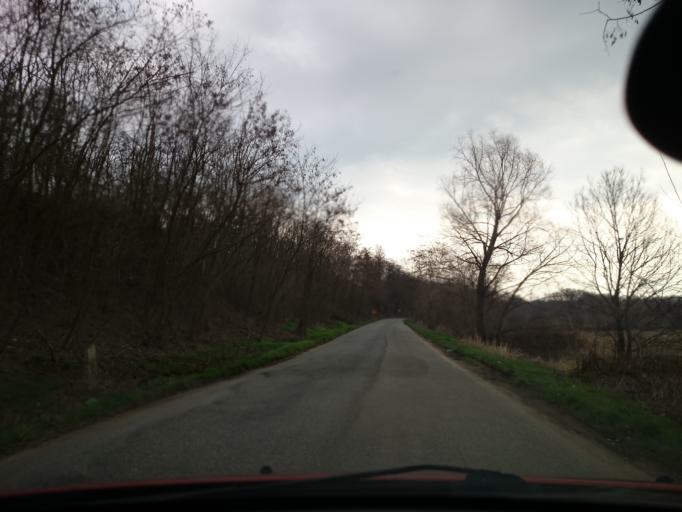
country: PL
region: Lower Silesian Voivodeship
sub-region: Powiat zabkowicki
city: Zabkowice Slaskie
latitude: 50.5273
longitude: 16.8139
